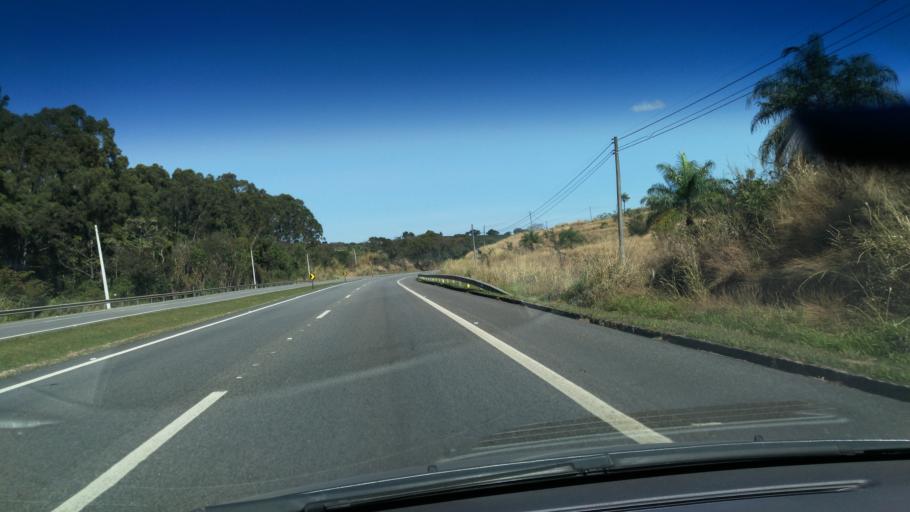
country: BR
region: Sao Paulo
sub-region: Santo Antonio Do Jardim
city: Espirito Santo do Pinhal
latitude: -22.2162
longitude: -46.7858
